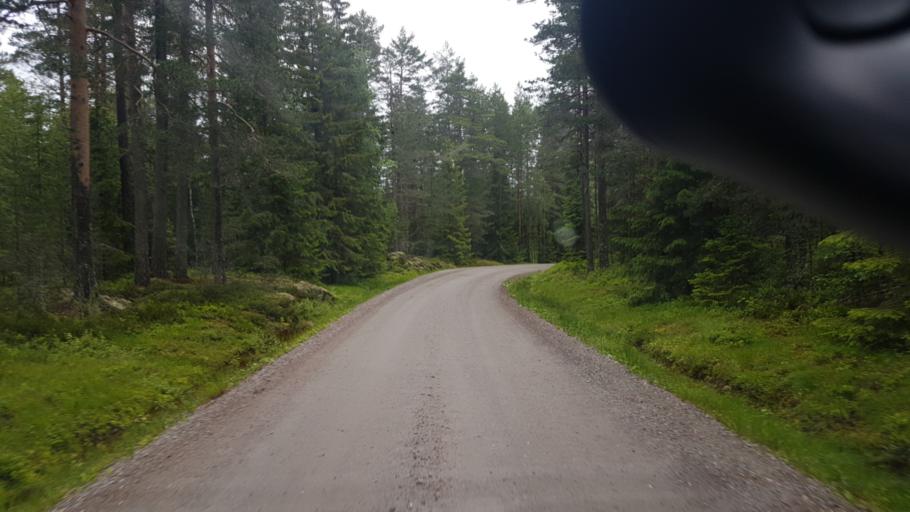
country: NO
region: Ostfold
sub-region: Romskog
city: Romskog
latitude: 59.7137
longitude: 12.0163
